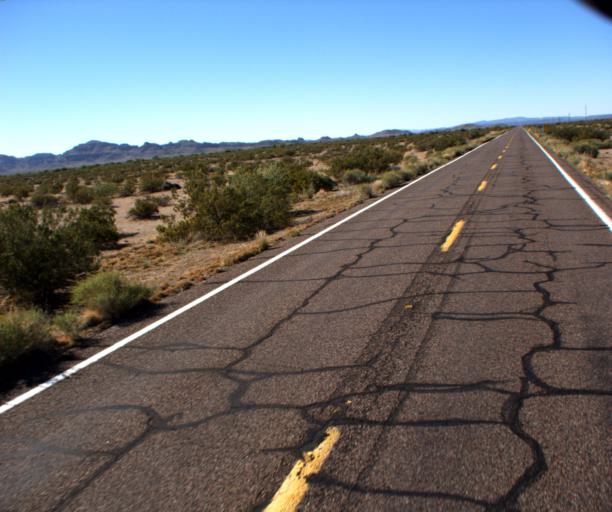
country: US
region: Arizona
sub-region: Maricopa County
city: Gila Bend
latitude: 32.7419
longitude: -112.8303
